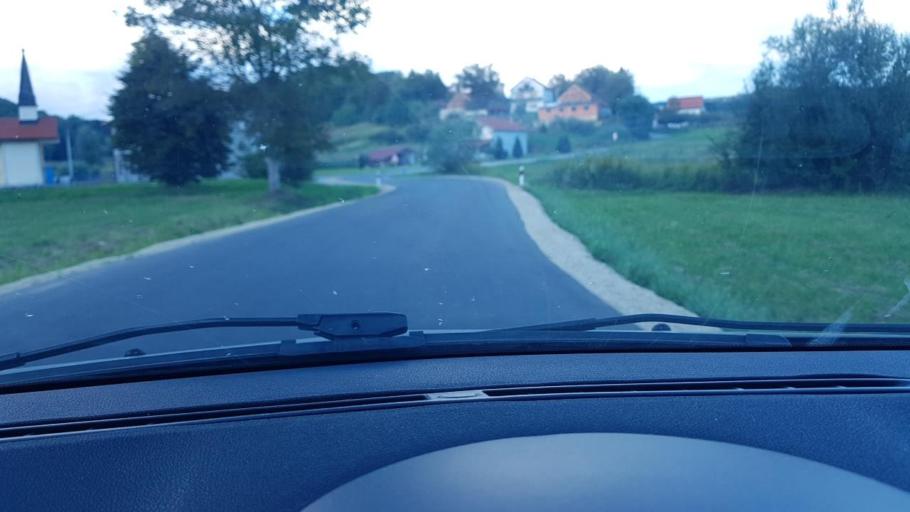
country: HR
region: Krapinsko-Zagorska
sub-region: Grad Krapina
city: Krapina
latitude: 46.1444
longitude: 15.8179
